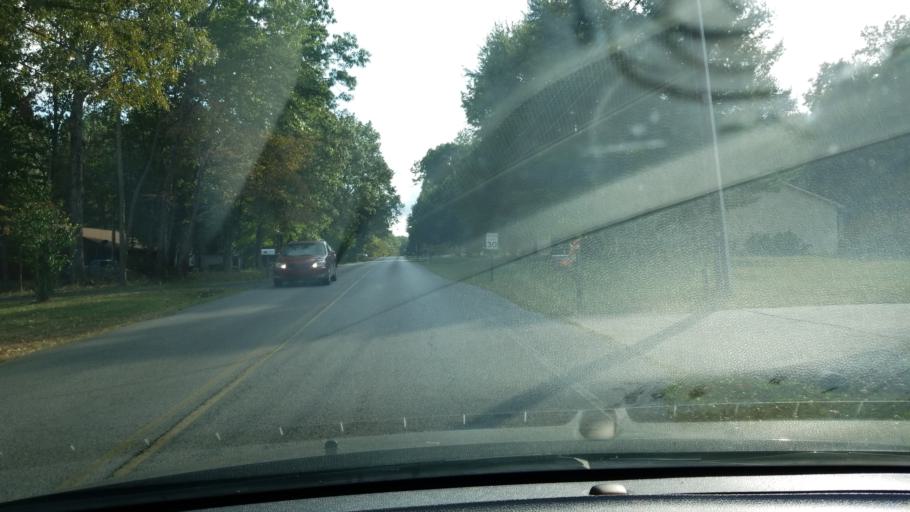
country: US
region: Tennessee
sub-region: Cumberland County
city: Crossville
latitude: 35.9493
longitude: -85.0571
